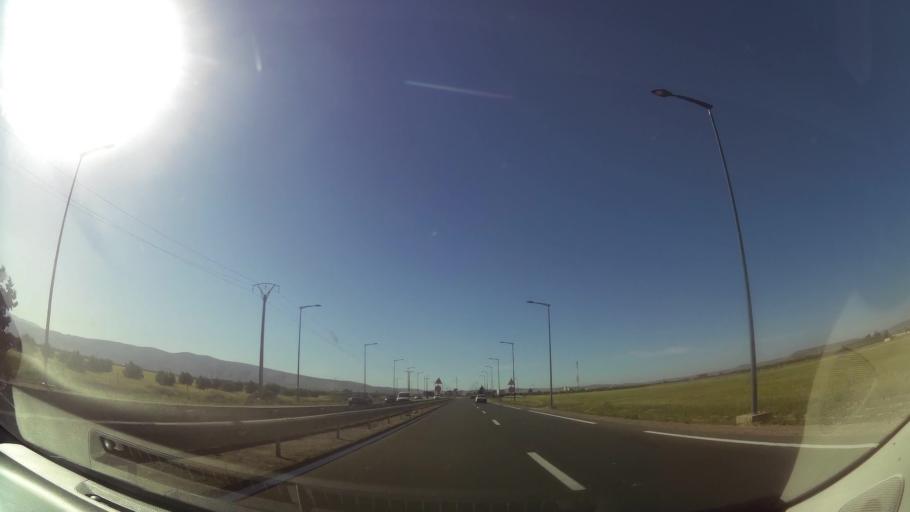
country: MA
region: Oriental
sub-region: Berkane-Taourirt
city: Ahfir
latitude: 34.8386
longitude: -1.9799
